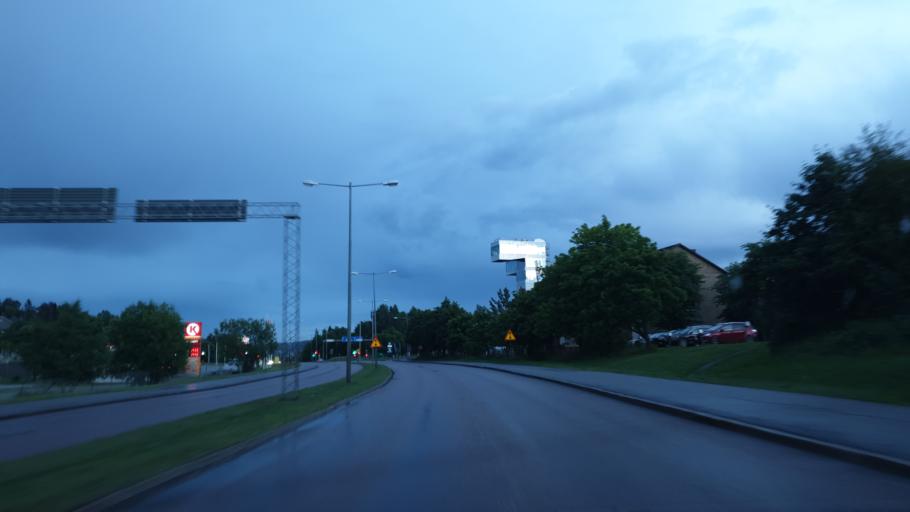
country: SE
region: Vaesternorrland
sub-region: OErnskoeldsviks Kommun
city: Ornskoldsvik
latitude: 63.2979
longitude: 18.7182
